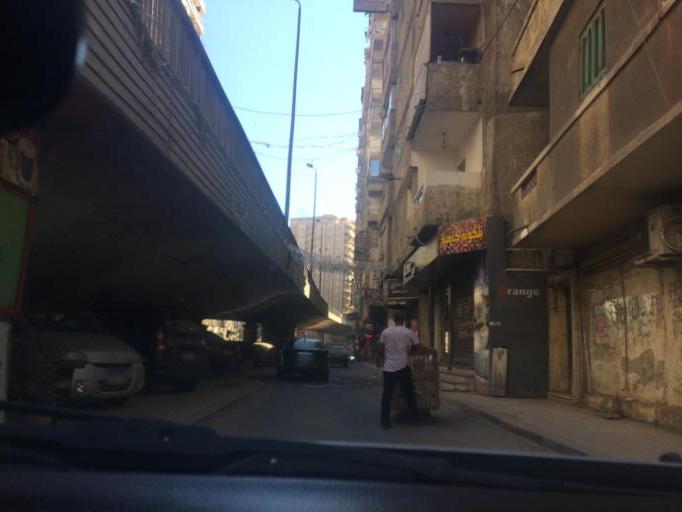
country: EG
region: Alexandria
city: Alexandria
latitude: 31.2688
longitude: 30.0009
